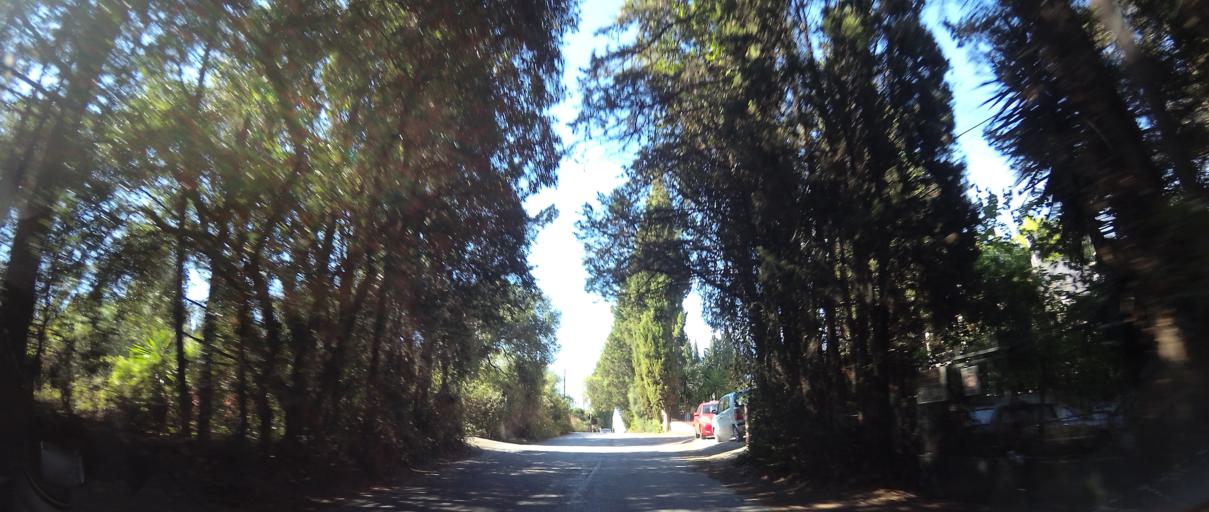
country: GR
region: Ionian Islands
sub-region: Nomos Kerkyras
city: Kontokali
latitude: 39.6421
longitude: 19.8513
